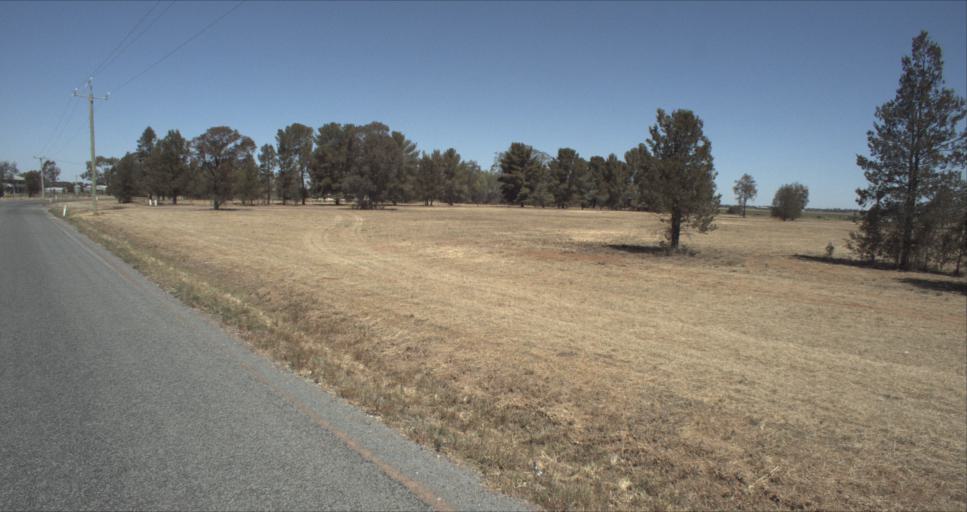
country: AU
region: New South Wales
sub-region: Leeton
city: Leeton
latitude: -34.5239
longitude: 146.4425
